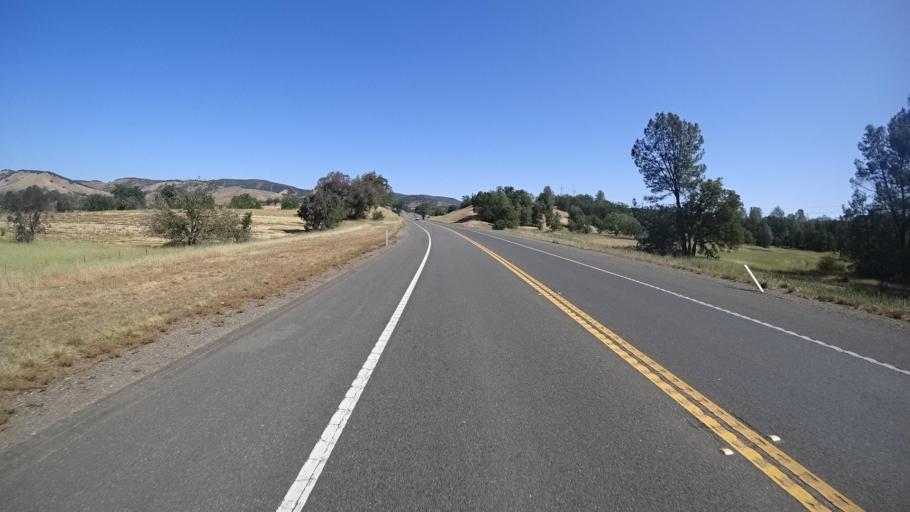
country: US
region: California
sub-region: Lake County
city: Clearlake
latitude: 38.9722
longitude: -122.6127
